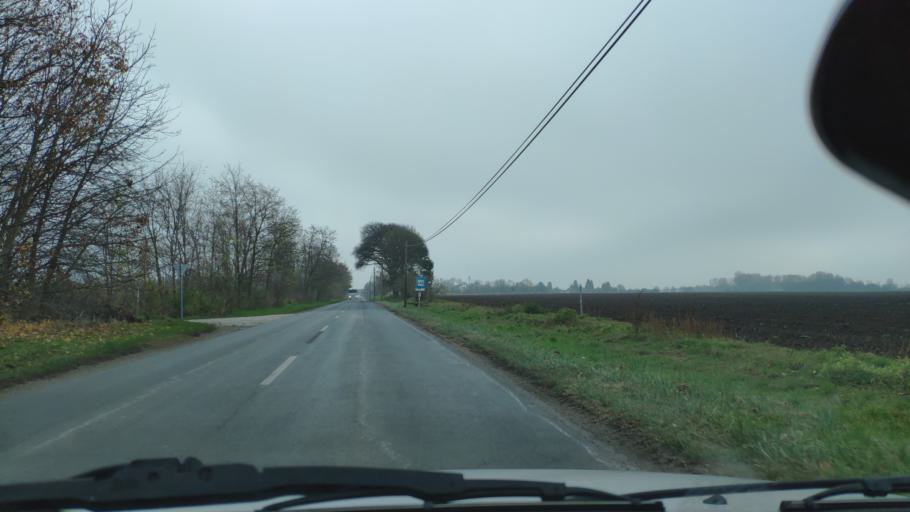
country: HU
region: Somogy
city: Balatonbereny
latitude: 46.6806
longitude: 17.2851
